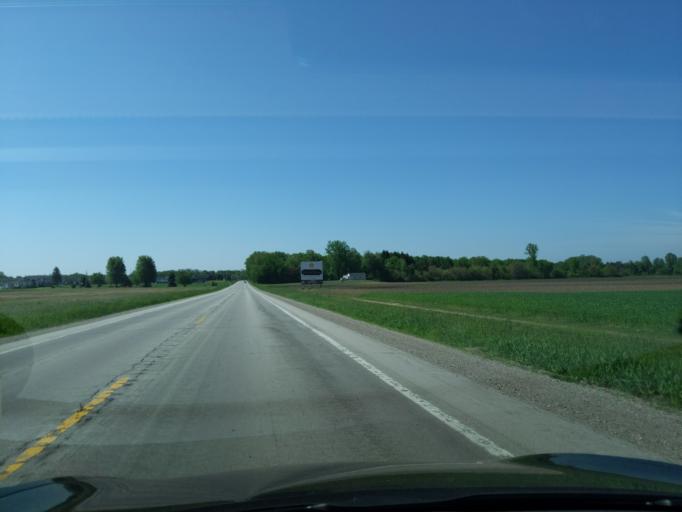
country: US
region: Michigan
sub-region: Ingham County
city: Stockbridge
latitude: 42.4647
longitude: -84.1901
